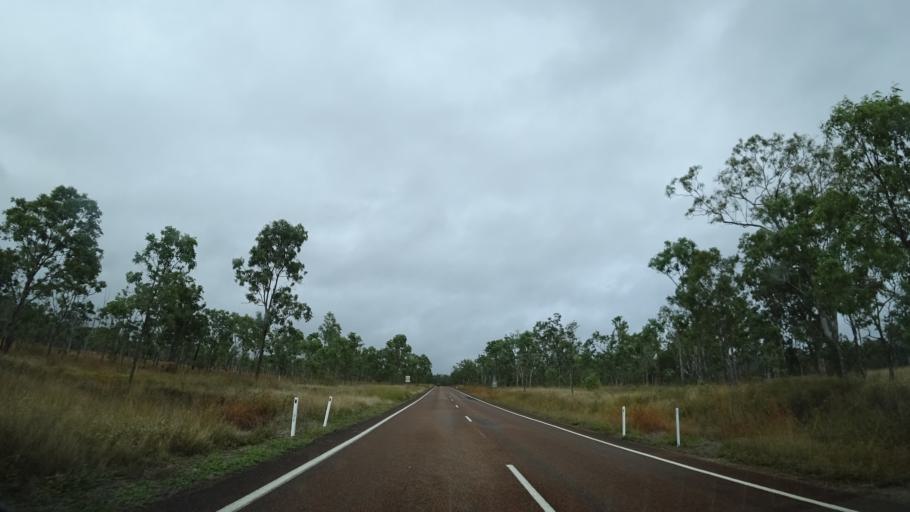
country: AU
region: Queensland
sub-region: Tablelands
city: Ravenshoe
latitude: -17.6732
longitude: 145.2372
